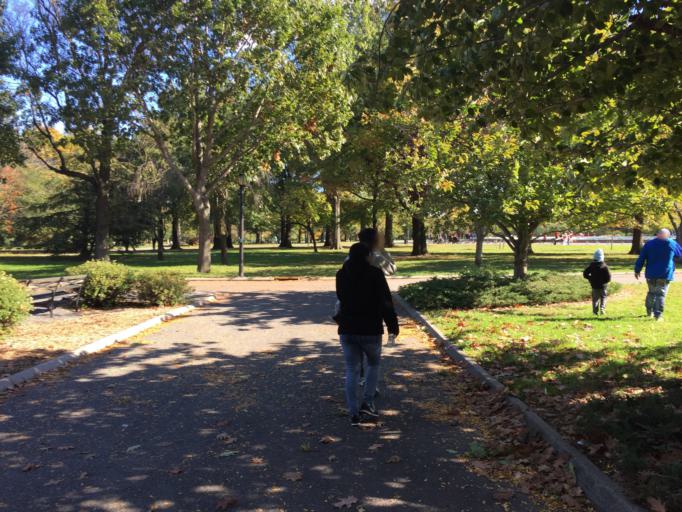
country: US
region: New York
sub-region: Queens County
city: Borough of Queens
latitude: 40.7466
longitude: -73.8466
